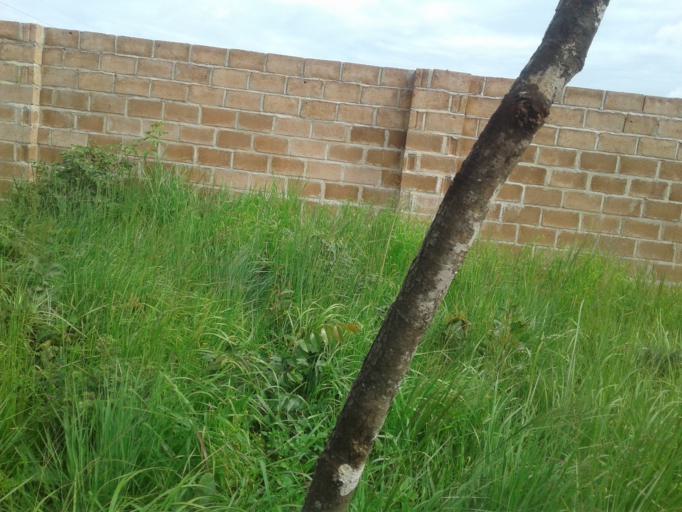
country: CD
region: Katanga
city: Lubumbashi
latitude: -11.4657
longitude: 27.5461
